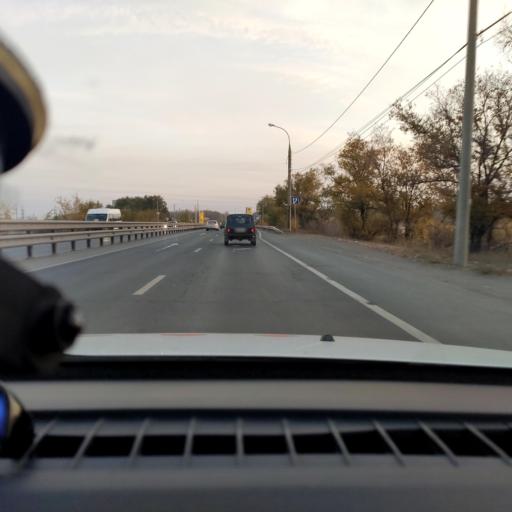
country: RU
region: Samara
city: Samara
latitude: 53.1226
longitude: 50.1687
